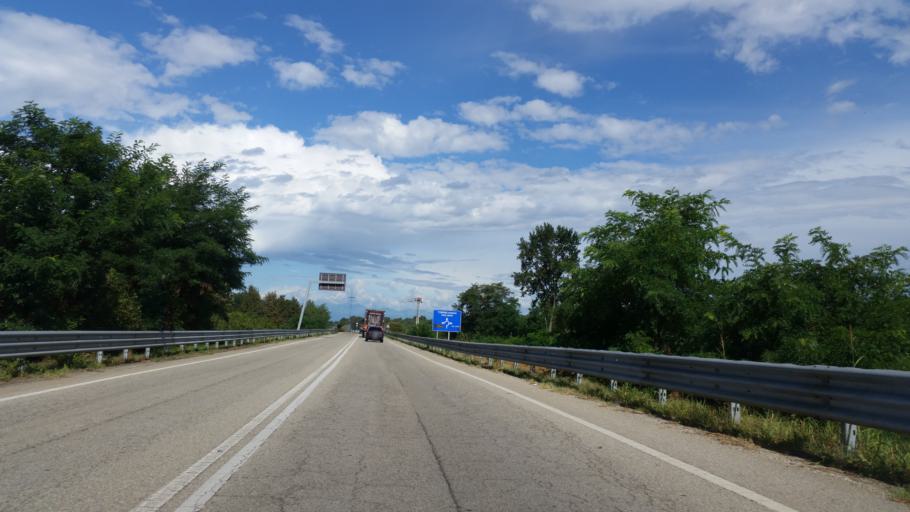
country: IT
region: Piedmont
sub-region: Provincia di Cuneo
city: Monta
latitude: 44.8225
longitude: 7.9462
